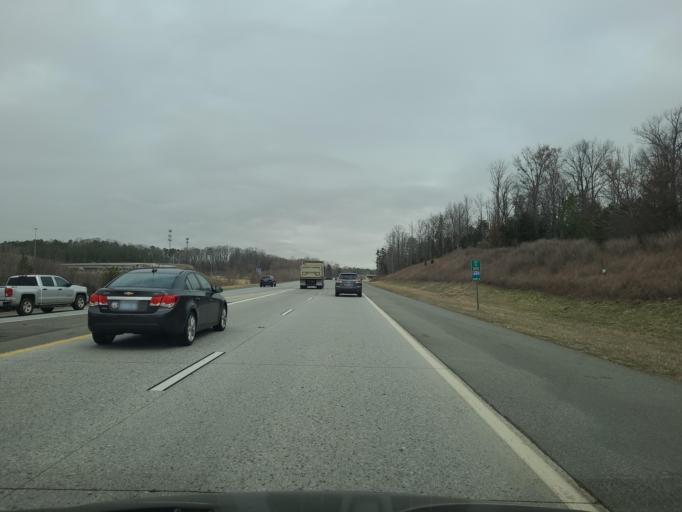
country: US
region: North Carolina
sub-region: Cabarrus County
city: Harrisburg
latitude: 35.3477
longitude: -80.7299
